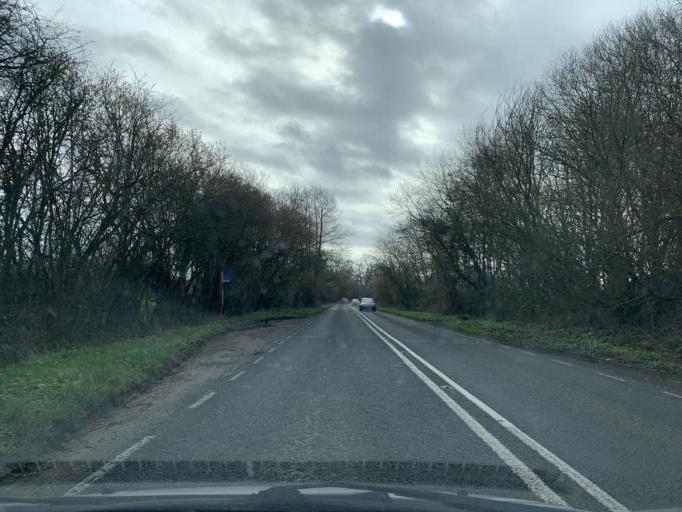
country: GB
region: England
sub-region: Wiltshire
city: Downton
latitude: 50.9773
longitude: -1.7641
